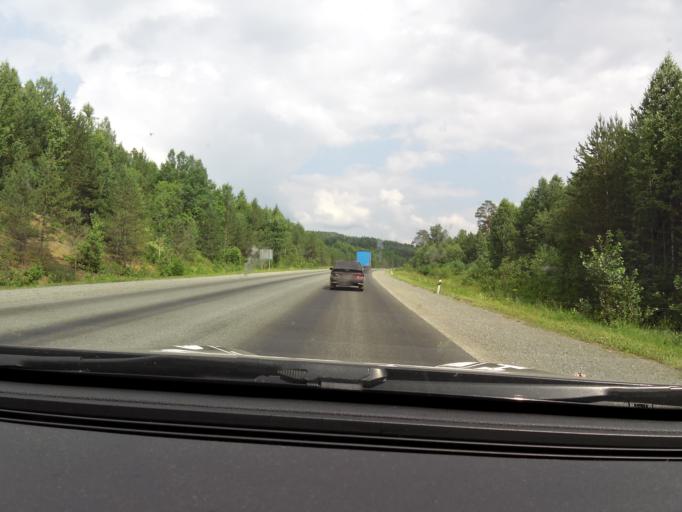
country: RU
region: Sverdlovsk
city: Ufimskiy
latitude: 56.7750
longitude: 58.2243
